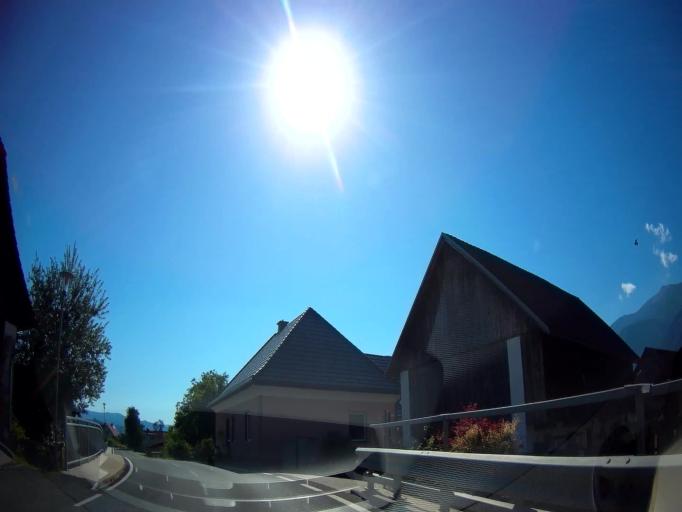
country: AT
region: Carinthia
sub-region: Politischer Bezirk Volkermarkt
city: Globasnitz
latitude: 46.5714
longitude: 14.7092
